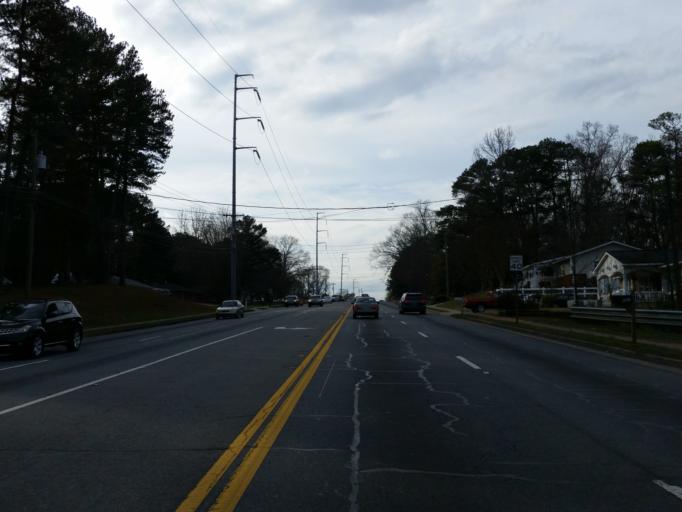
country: US
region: Georgia
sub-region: Cobb County
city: Fair Oaks
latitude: 33.8948
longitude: -84.5583
